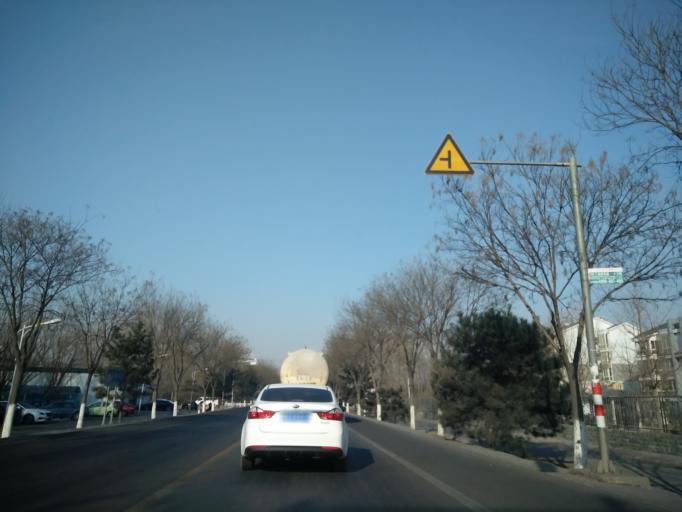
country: CN
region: Beijing
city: Qingyundian
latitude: 39.6728
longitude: 116.5208
